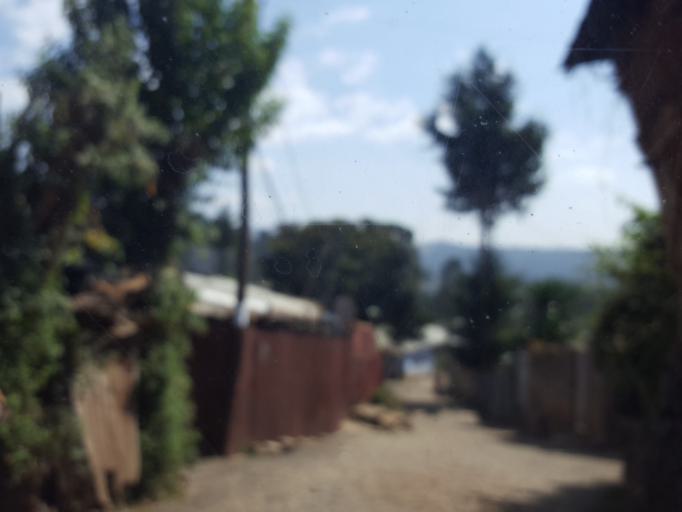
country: ET
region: Adis Abeba
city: Addis Ababa
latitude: 9.0632
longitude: 38.7618
